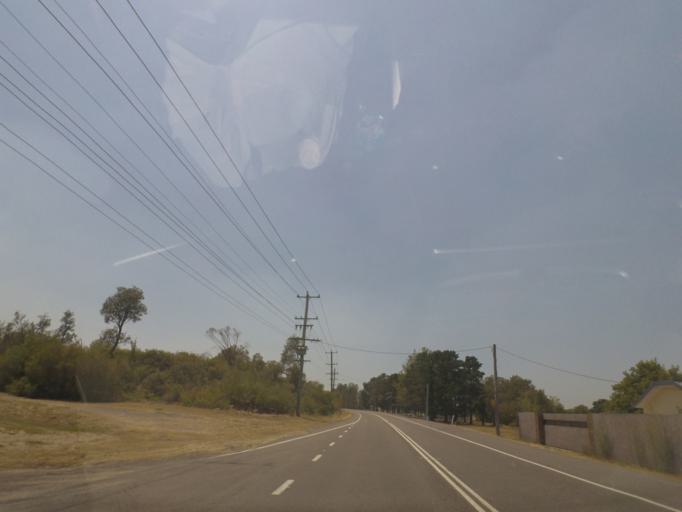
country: AU
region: New South Wales
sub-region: Port Stephens Shire
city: Medowie
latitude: -32.8071
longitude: 151.8728
